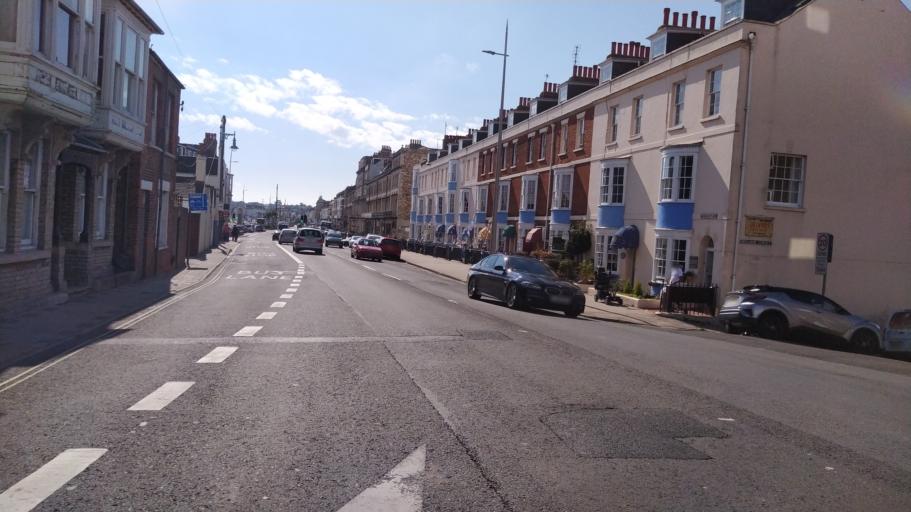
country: GB
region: England
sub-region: Dorset
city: Weymouth
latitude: 50.6186
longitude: -2.4508
